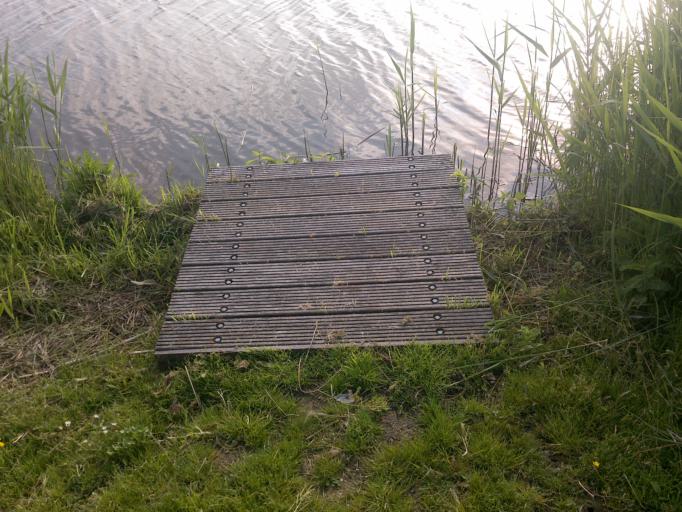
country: NL
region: Friesland
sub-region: Gemeente Boarnsterhim
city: Reduzum
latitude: 53.1216
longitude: 5.7559
